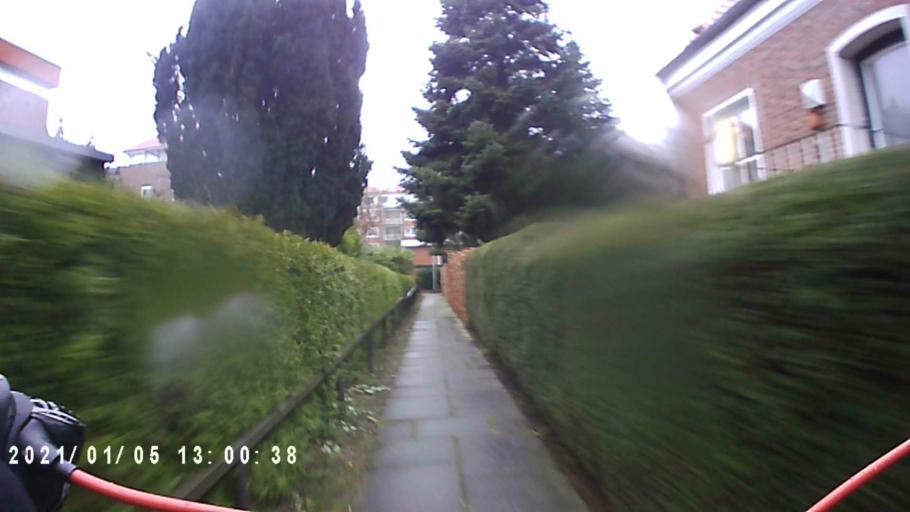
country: DE
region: Lower Saxony
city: Leer
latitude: 53.2307
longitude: 7.4761
